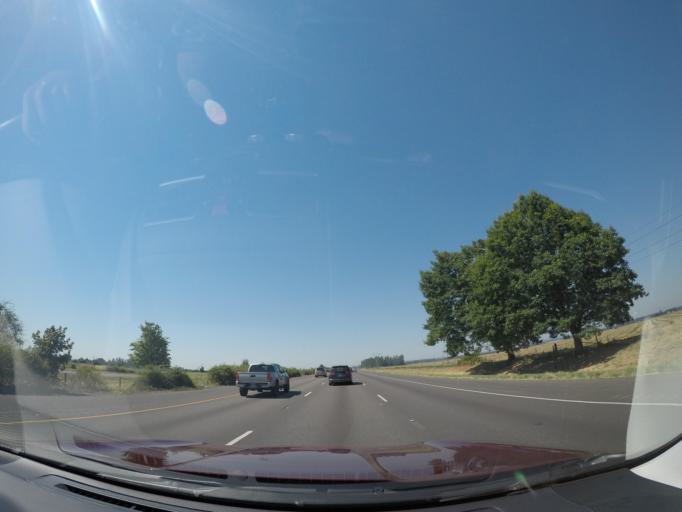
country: US
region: Oregon
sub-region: Marion County
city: Gervais
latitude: 45.1333
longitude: -122.8974
